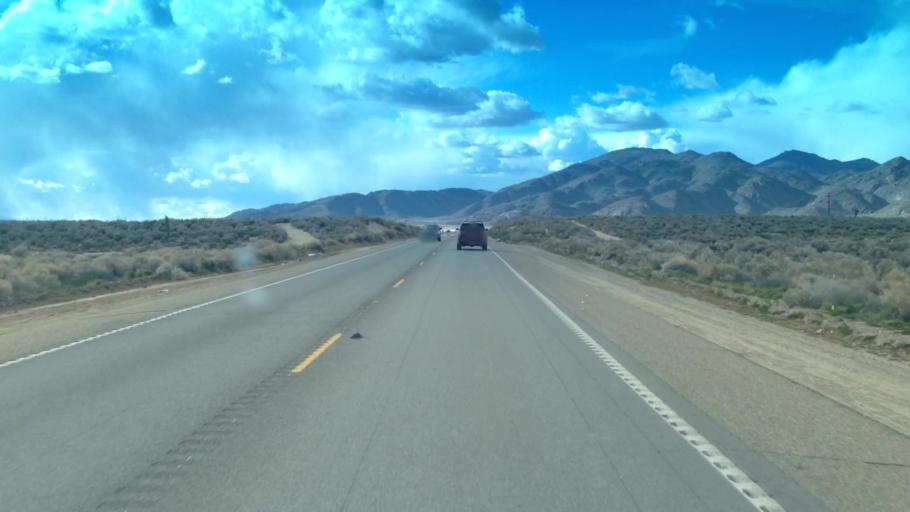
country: US
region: California
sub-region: San Bernardino County
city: Lucerne Valley
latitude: 34.4488
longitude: -117.0006
